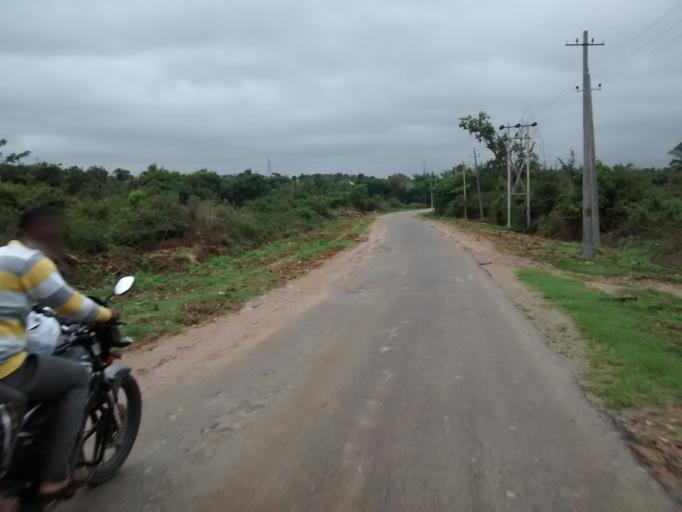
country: IN
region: Karnataka
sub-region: Hassan
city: Hassan
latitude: 12.9437
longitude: 76.1636
